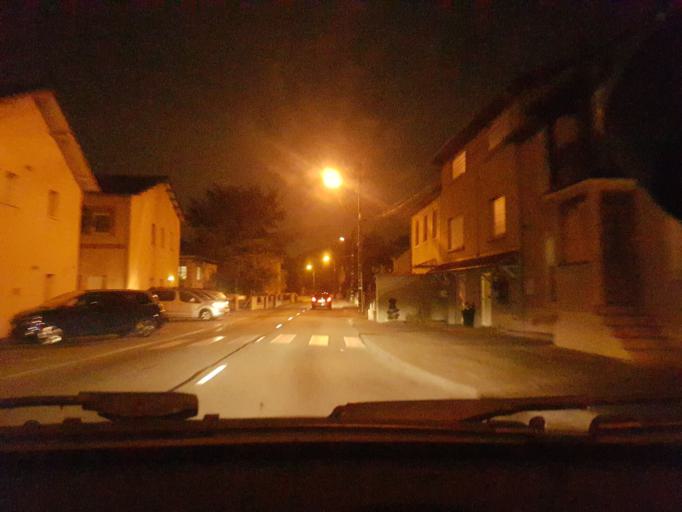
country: FR
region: Franche-Comte
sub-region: Territoire de Belfort
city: Danjoutin
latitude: 47.6192
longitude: 6.8670
